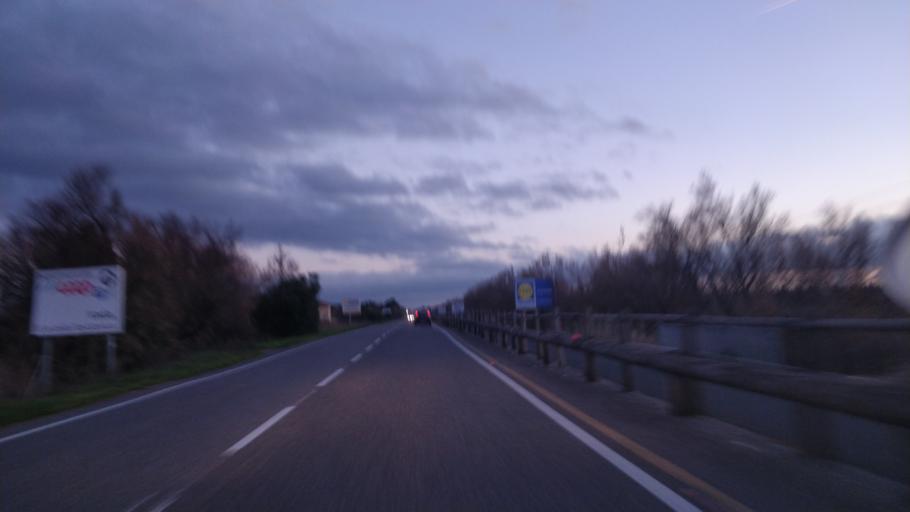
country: IT
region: Tuscany
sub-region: Provincia di Livorno
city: Vada
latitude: 43.3685
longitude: 10.4506
